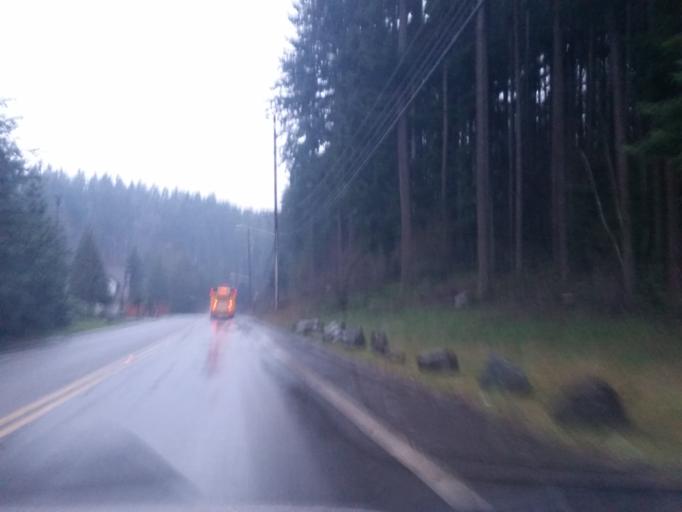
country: US
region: Washington
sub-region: Snohomish County
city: Meadowdale
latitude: 47.8728
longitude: -122.3092
